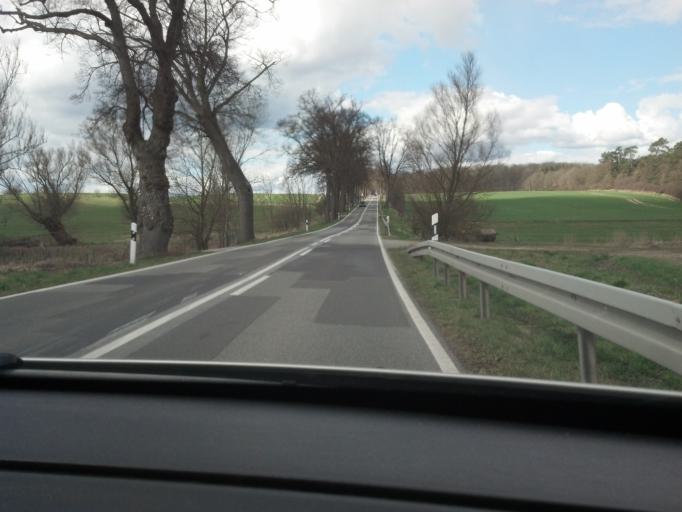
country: DE
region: Mecklenburg-Vorpommern
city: Loitz
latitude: 53.4694
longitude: 13.3525
